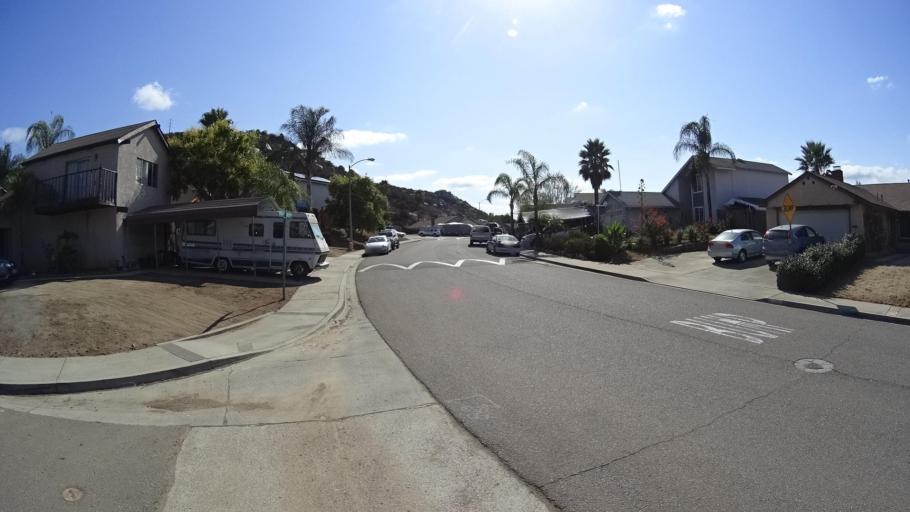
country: US
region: California
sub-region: San Diego County
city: Eucalyptus Hills
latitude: 32.8667
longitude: -116.9595
